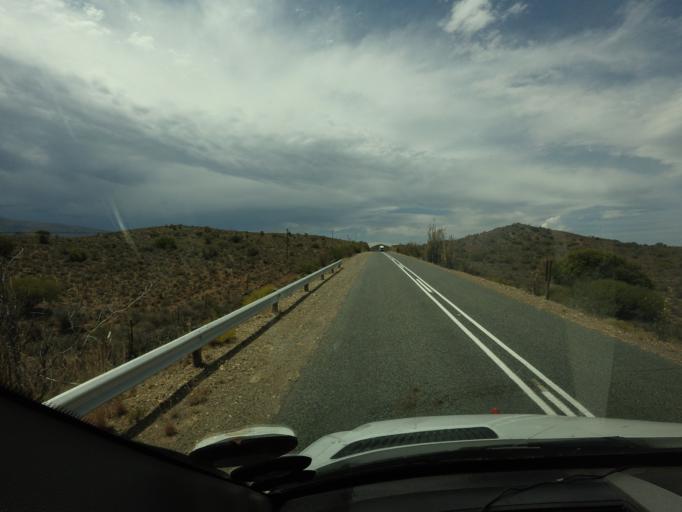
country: ZA
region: Western Cape
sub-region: Eden District Municipality
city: Ladismith
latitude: -33.6360
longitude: 21.0374
